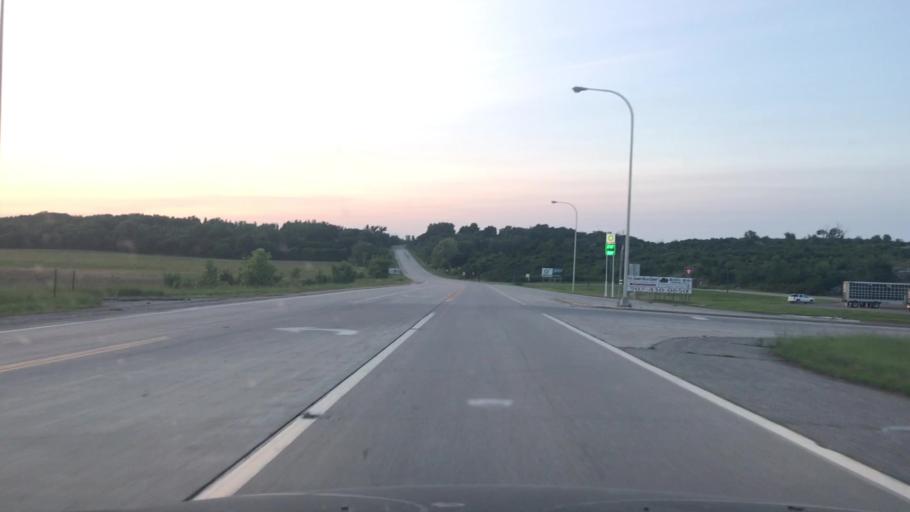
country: US
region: Minnesota
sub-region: Redwood County
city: Redwood Falls
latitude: 44.5488
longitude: -94.9949
